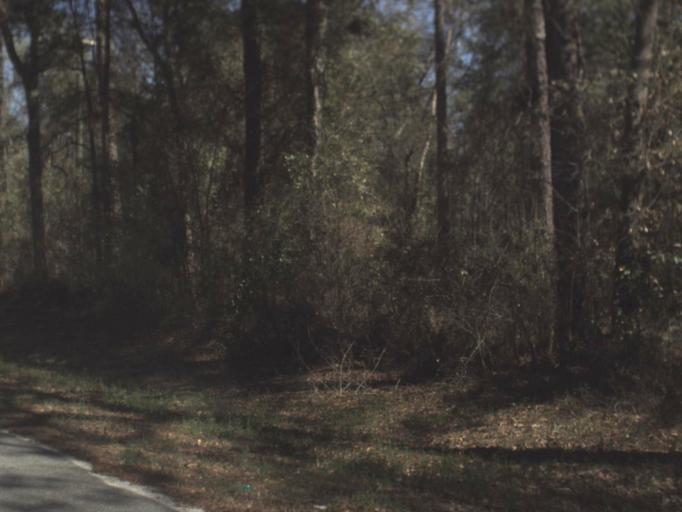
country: US
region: Florida
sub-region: Leon County
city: Woodville
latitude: 30.3044
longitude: -84.3118
